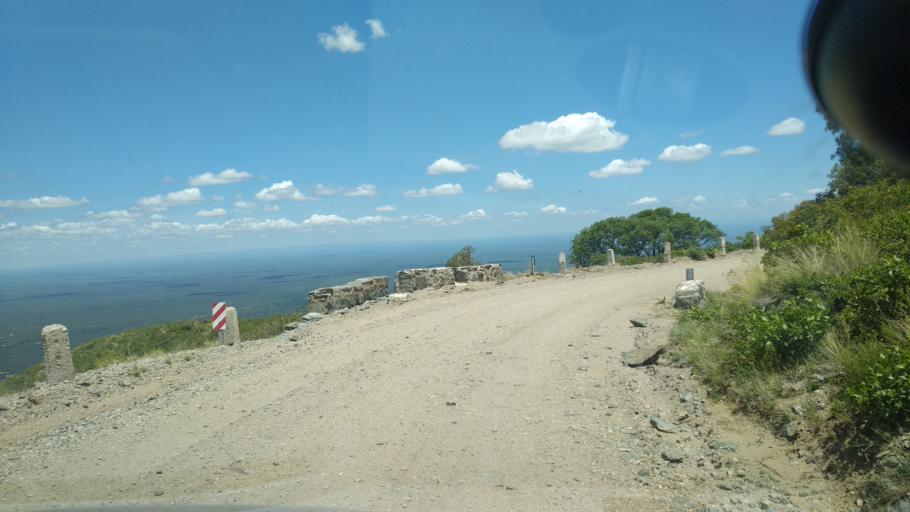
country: AR
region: Cordoba
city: Salsacate
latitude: -31.3798
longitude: -65.4018
